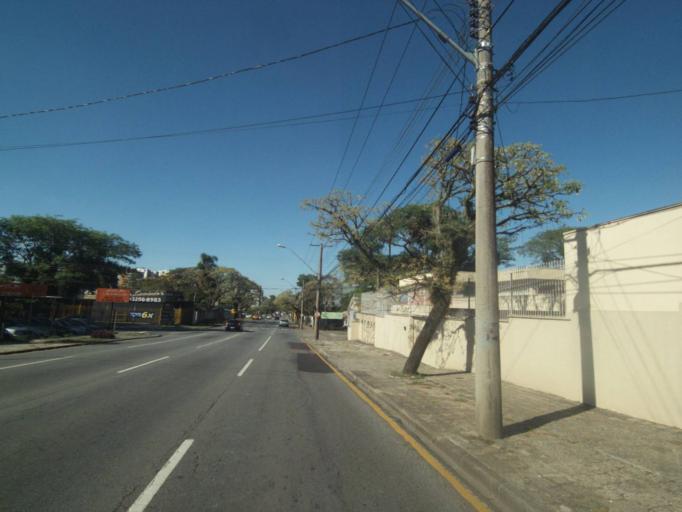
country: BR
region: Parana
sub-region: Curitiba
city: Curitiba
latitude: -25.3939
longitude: -49.2394
